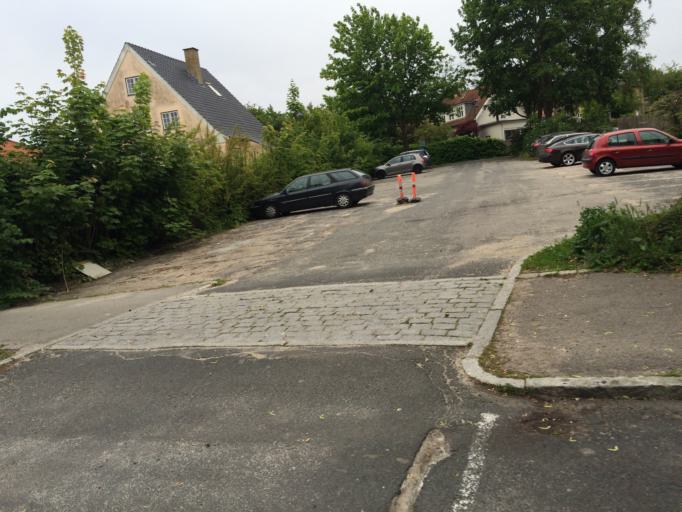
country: DK
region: Capital Region
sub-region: Lyngby-Tarbaek Kommune
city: Kongens Lyngby
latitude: 55.7460
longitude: 12.5436
